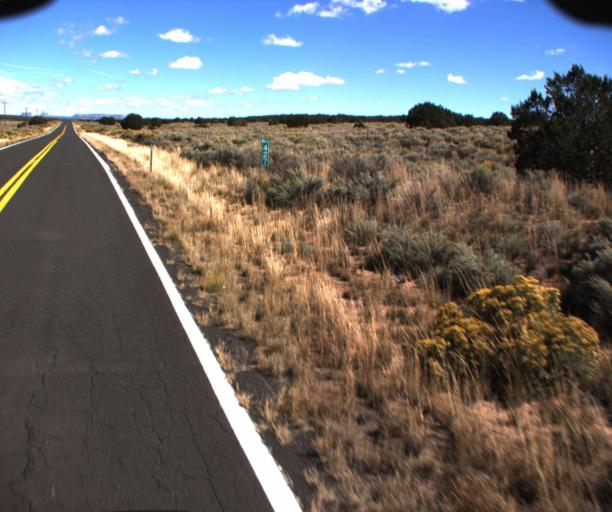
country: US
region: New Mexico
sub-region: McKinley County
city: Zuni Pueblo
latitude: 34.9960
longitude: -109.0953
